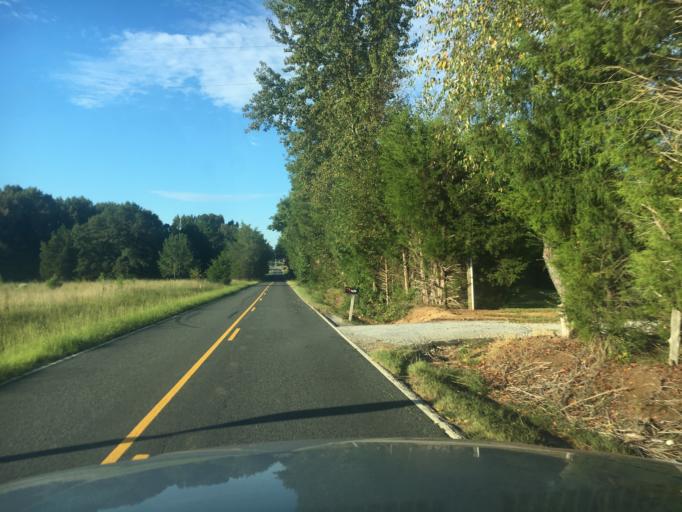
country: US
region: South Carolina
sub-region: Spartanburg County
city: Woodruff
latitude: 34.6360
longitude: -82.0278
